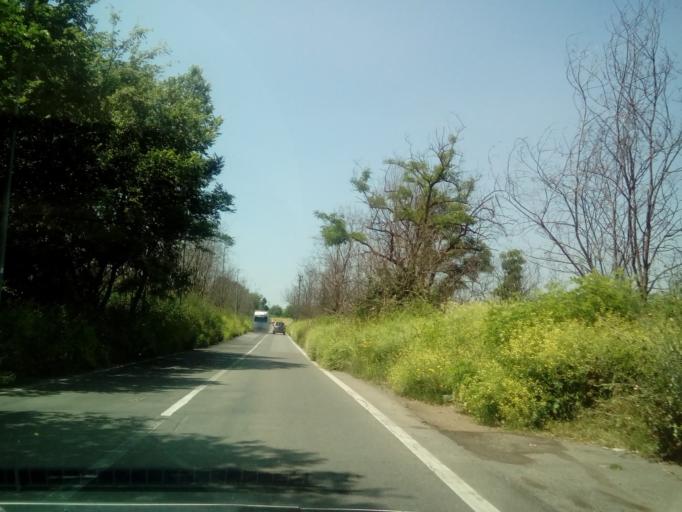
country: IT
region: Latium
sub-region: Citta metropolitana di Roma Capitale
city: Selcetta
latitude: 41.8027
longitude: 12.4759
